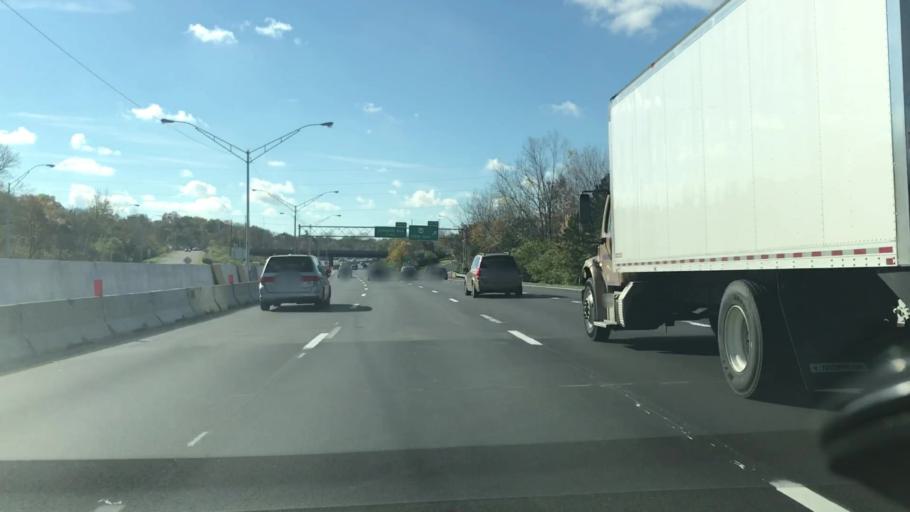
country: US
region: Ohio
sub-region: Franklin County
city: Bexley
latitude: 39.9888
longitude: -82.9383
